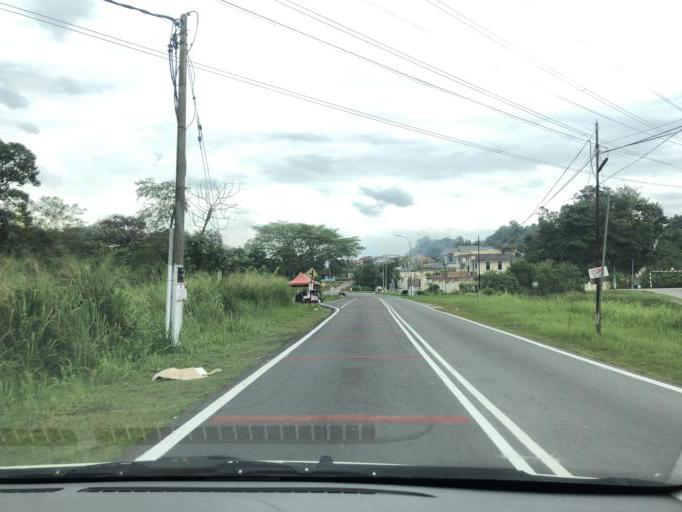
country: MY
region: Putrajaya
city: Putrajaya
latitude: 2.9180
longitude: 101.7534
